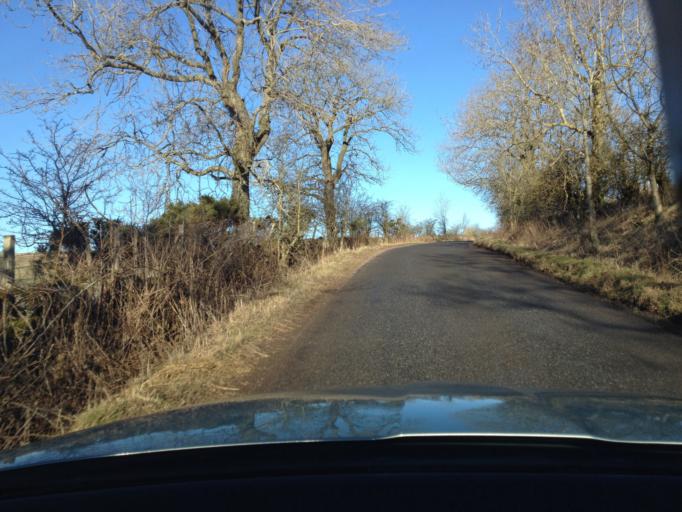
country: GB
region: Scotland
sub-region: Perth and Kinross
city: Bridge of Earn
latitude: 56.2938
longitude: -3.3971
